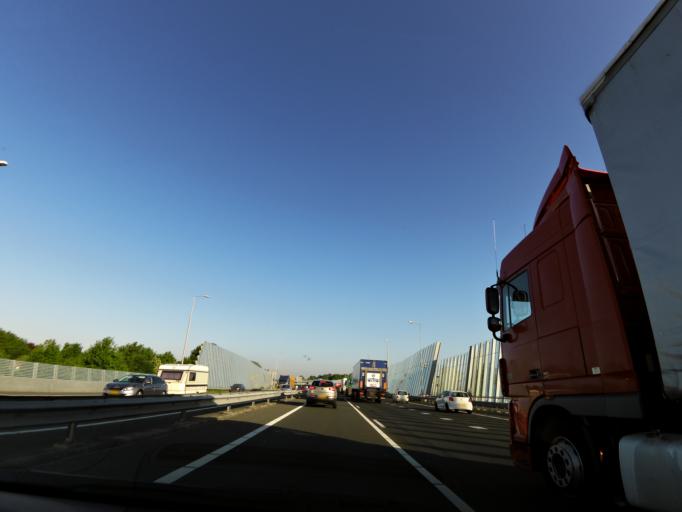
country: NL
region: Limburg
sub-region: Gemeente Venlo
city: Tegelen
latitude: 51.3567
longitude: 6.1444
